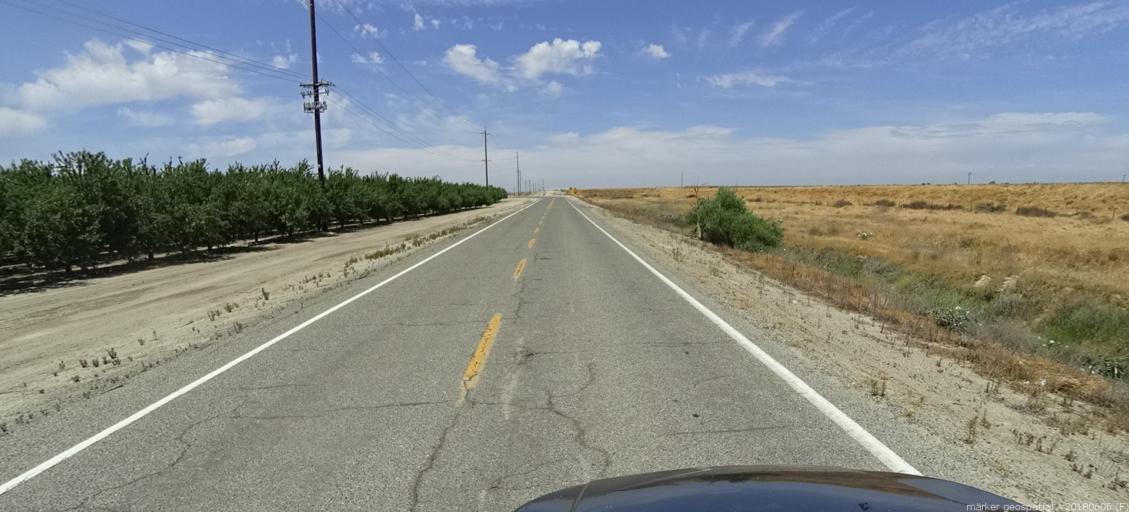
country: US
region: California
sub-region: Fresno County
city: Mendota
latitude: 36.8481
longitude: -120.3169
